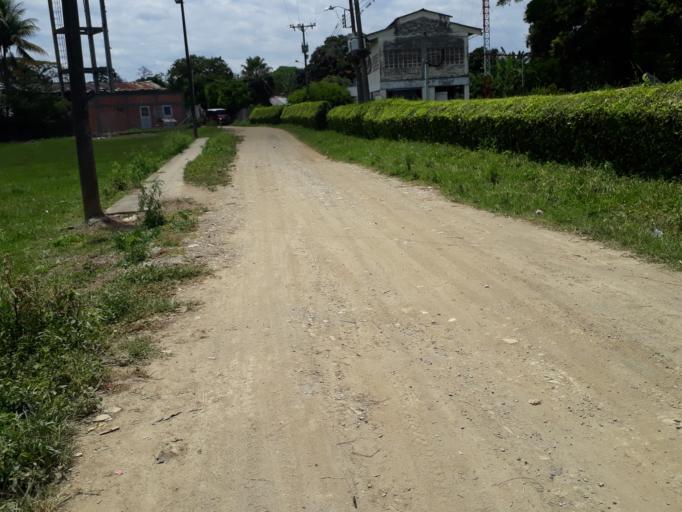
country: CO
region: Valle del Cauca
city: Cali
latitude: 3.3607
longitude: -76.4833
